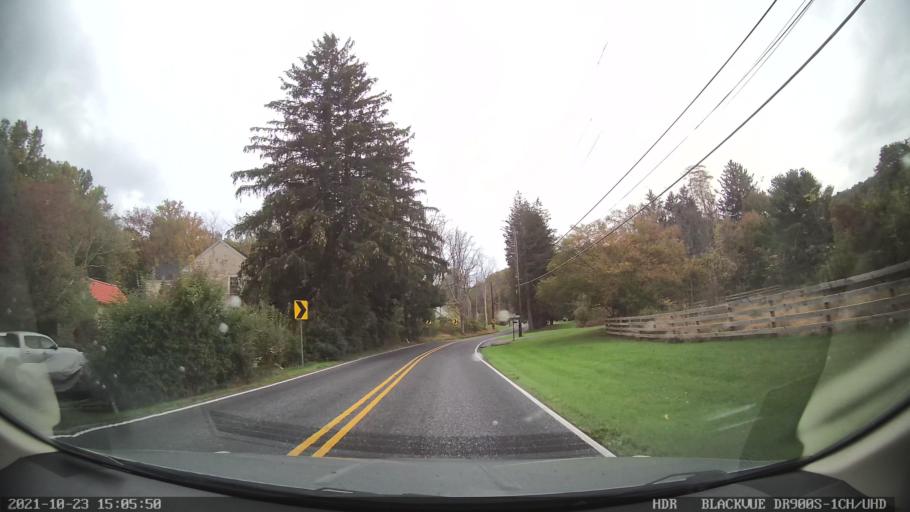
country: US
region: Pennsylvania
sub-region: Berks County
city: Bally
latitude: 40.4339
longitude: -75.5847
